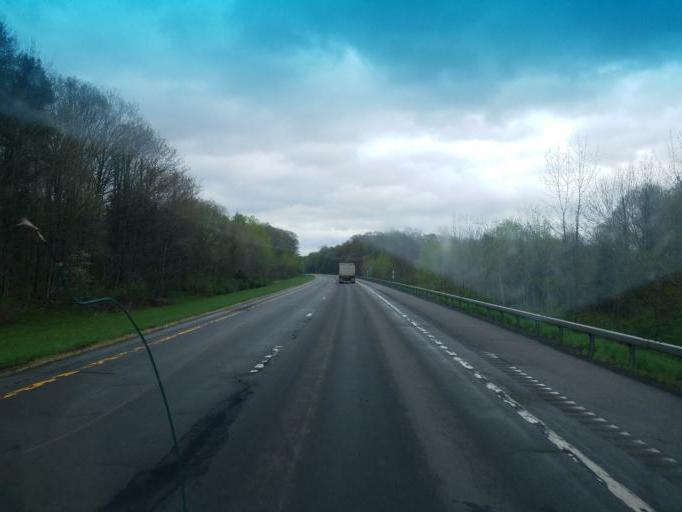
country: US
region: New York
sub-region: Chautauqua County
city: Falconer
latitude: 42.1340
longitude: -79.1409
